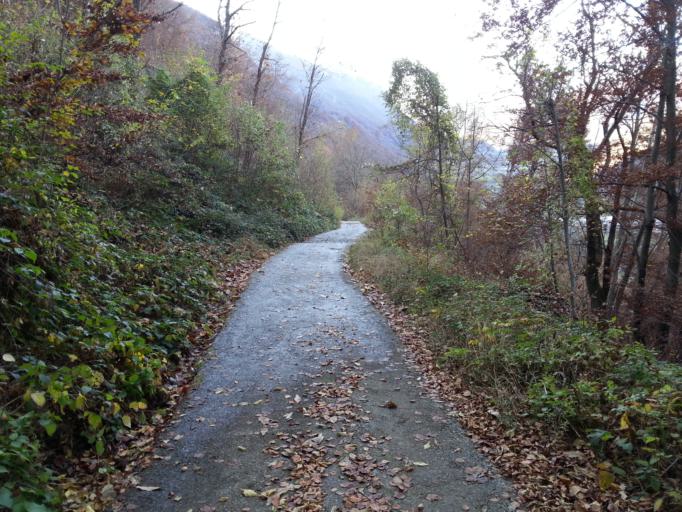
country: IT
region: Lombardy
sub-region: Provincia di Lecco
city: Primaluna
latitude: 45.9778
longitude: 9.4199
